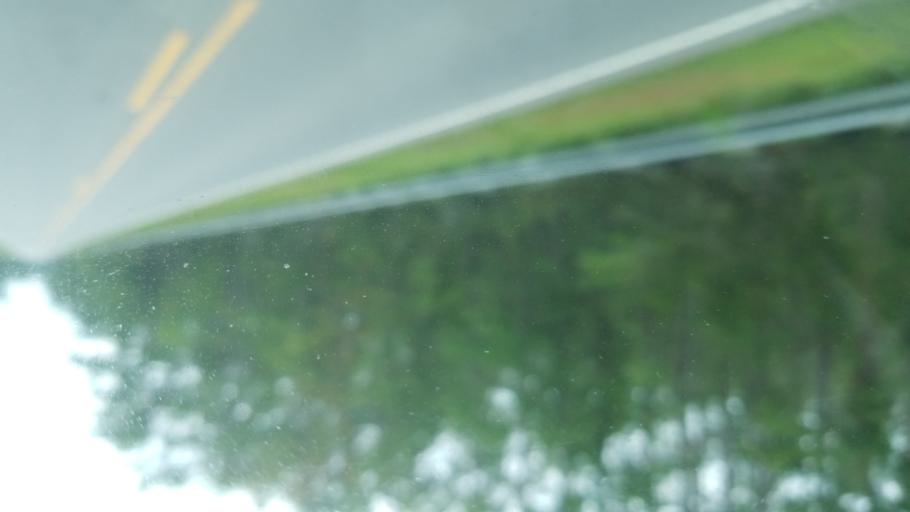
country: US
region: North Carolina
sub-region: Dare County
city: Manteo
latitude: 35.8820
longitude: -75.9487
